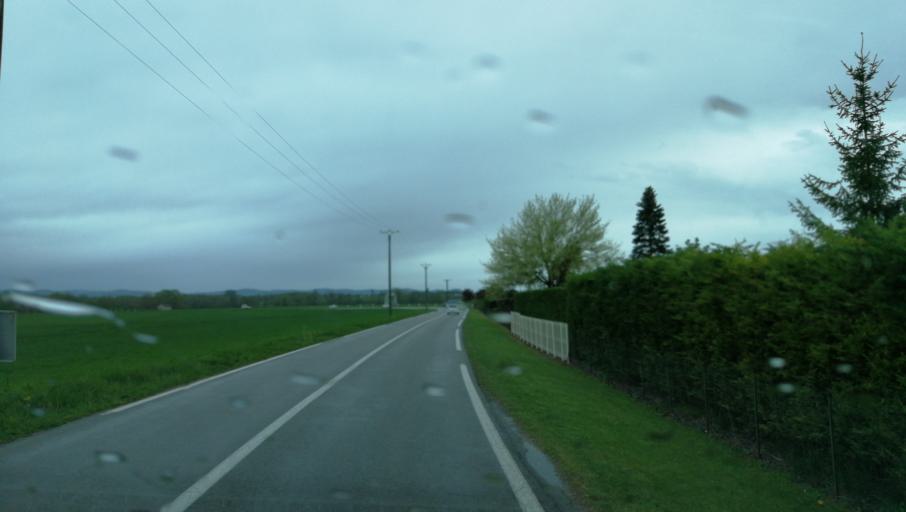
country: FR
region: Franche-Comte
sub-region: Departement du Jura
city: Bletterans
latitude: 46.7337
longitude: 5.4697
